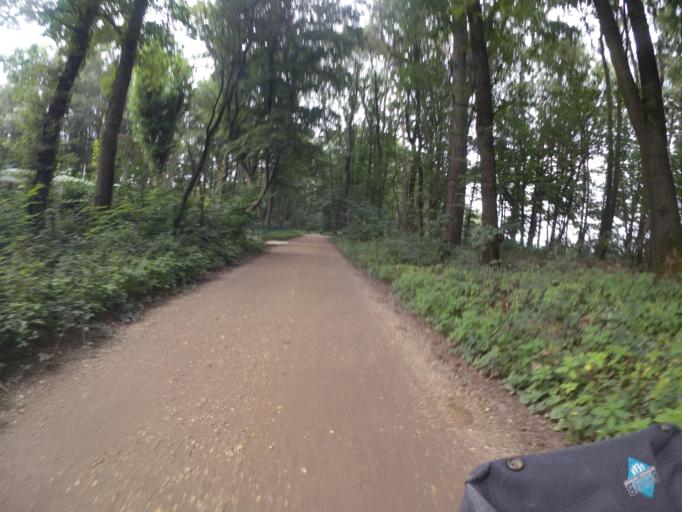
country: NL
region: Gelderland
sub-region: Gemeente Groesbeek
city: Bredeweg
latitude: 51.7574
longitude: 5.9135
